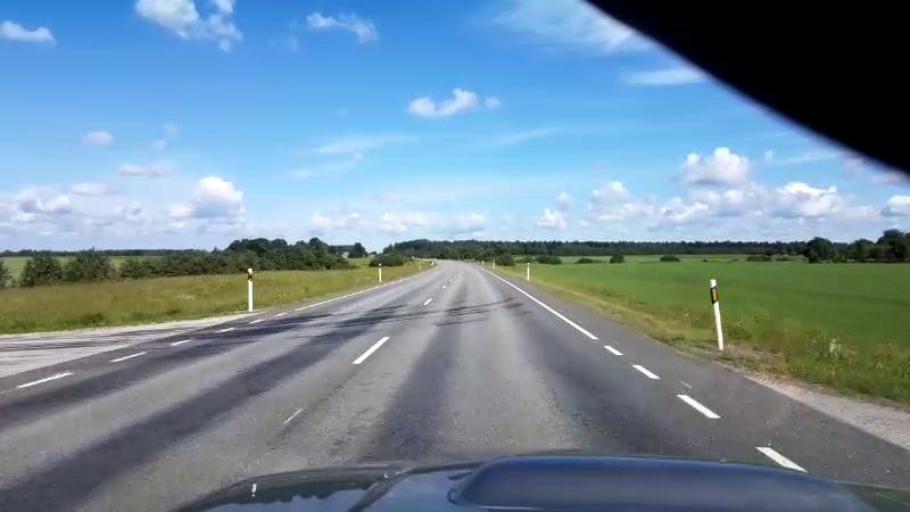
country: EE
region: Jaervamaa
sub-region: Jaerva-Jaani vald
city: Jarva-Jaani
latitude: 59.1492
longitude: 25.7702
